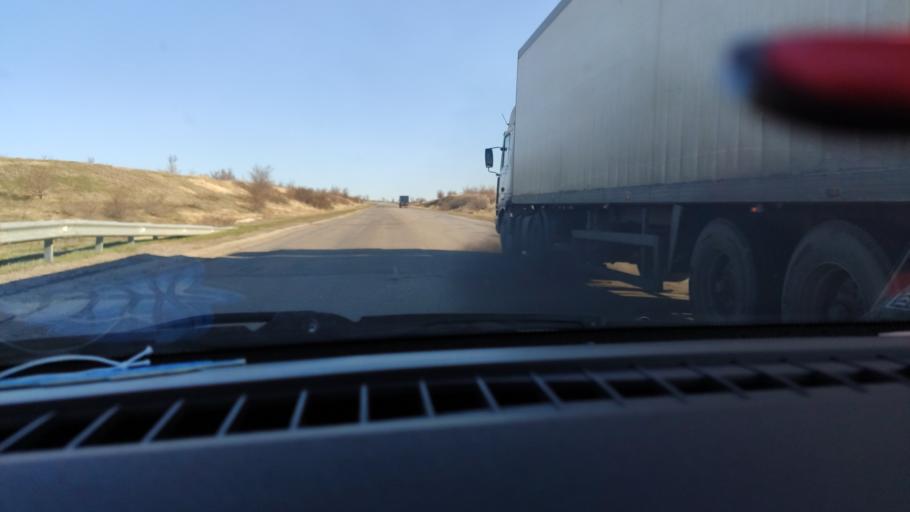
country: RU
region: Samara
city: Varlamovo
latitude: 53.0980
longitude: 48.3563
